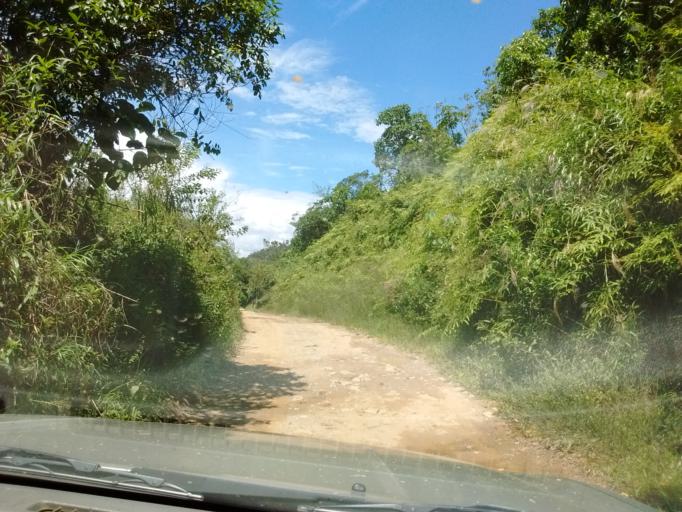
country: CO
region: Cauca
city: Villa Rica
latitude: 2.6380
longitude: -76.7705
